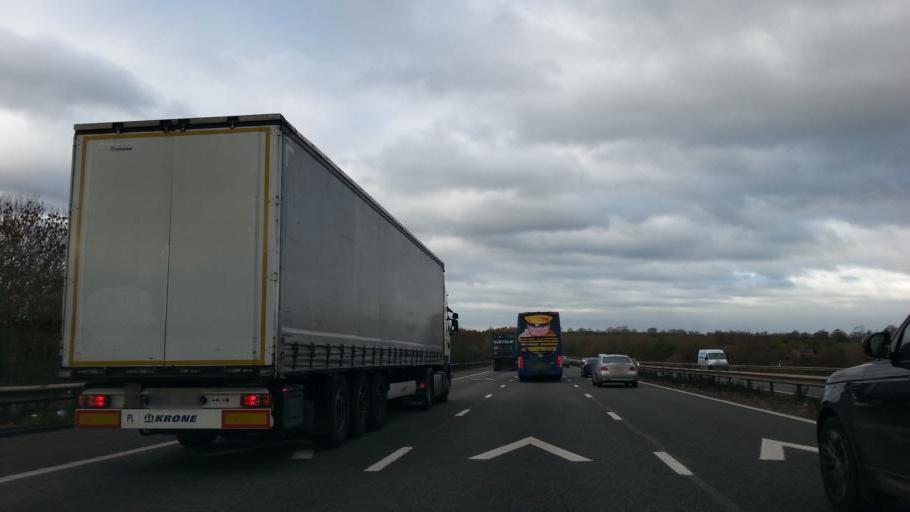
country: GB
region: England
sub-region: Warwickshire
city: Long Lawford
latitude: 52.4286
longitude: -1.3223
